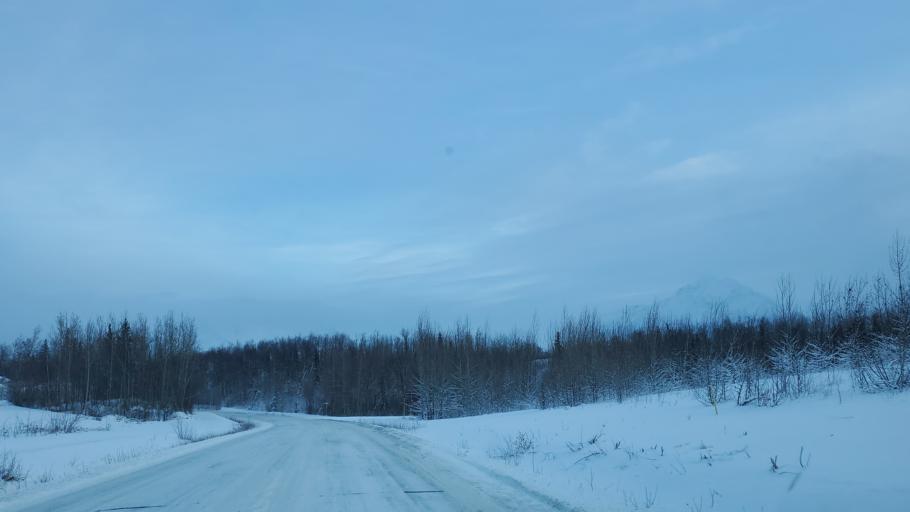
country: US
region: Alaska
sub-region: Matanuska-Susitna Borough
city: Lakes
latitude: 61.5482
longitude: -149.3138
